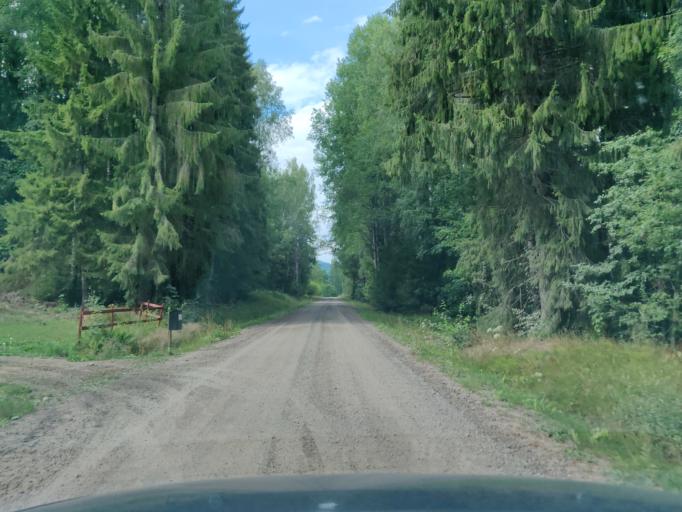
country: SE
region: Vaermland
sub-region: Hagfors Kommun
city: Ekshaerad
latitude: 60.0039
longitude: 13.4813
